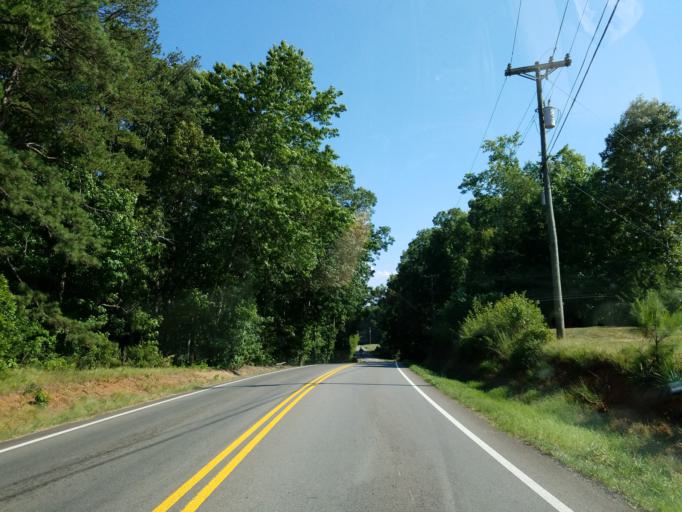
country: US
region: Georgia
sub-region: Fulton County
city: Milton
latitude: 34.2257
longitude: -84.2897
